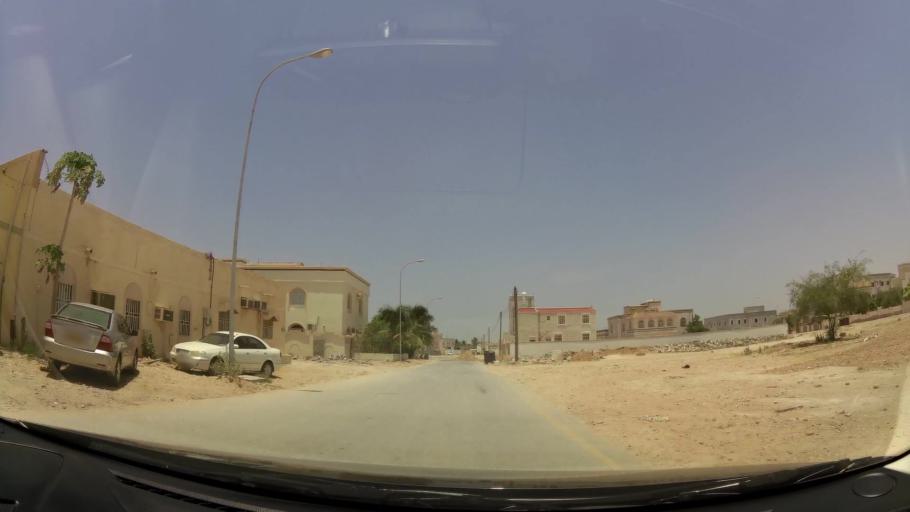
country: OM
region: Zufar
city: Salalah
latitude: 17.0810
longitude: 54.1518
